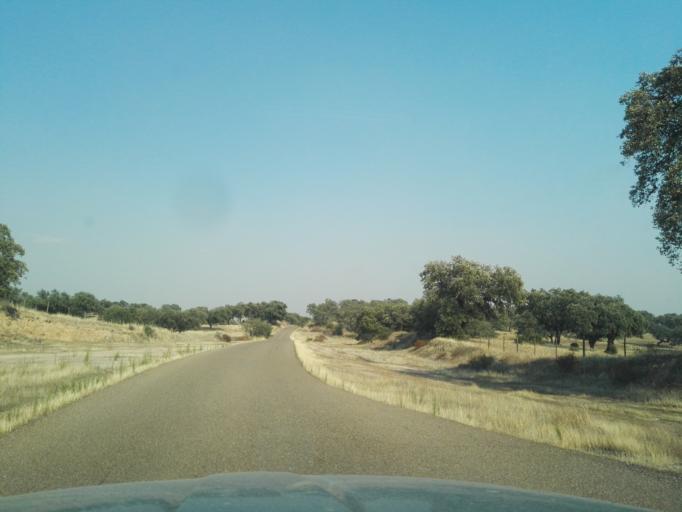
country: PT
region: Portalegre
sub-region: Campo Maior
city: Campo Maior
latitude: 38.9938
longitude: -7.1637
